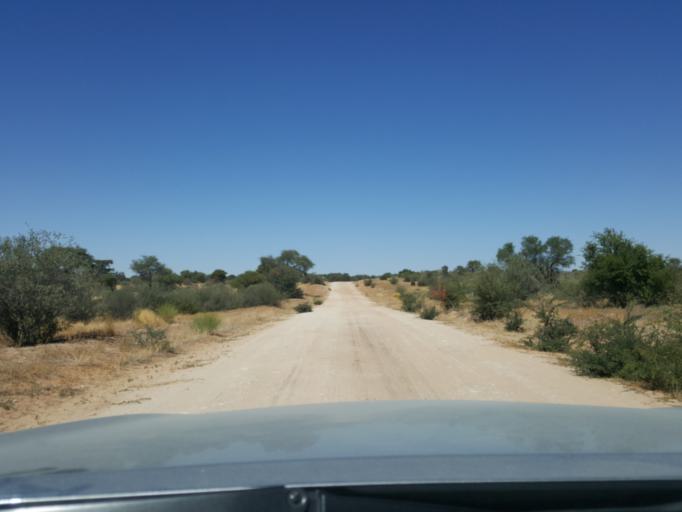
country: BW
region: Kgalagadi
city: Hukuntsi
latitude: -23.9794
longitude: 21.2077
